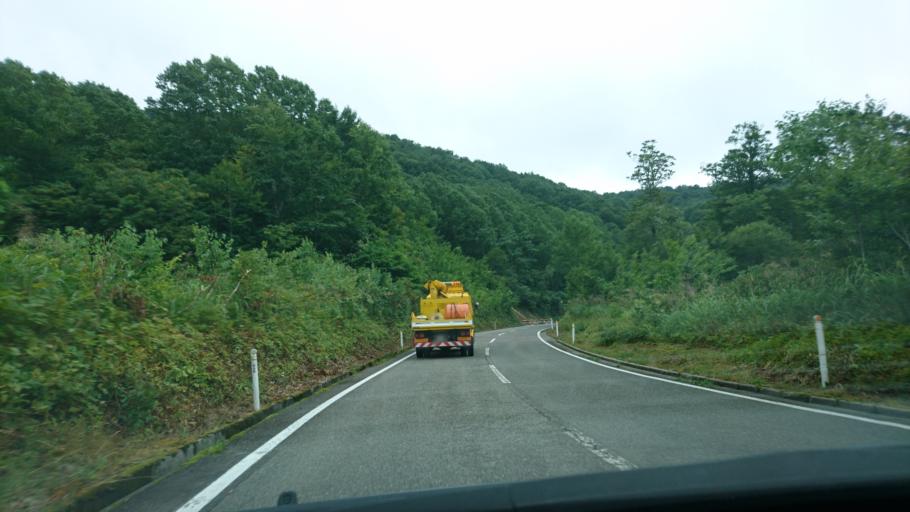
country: JP
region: Akita
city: Yuzawa
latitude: 38.9830
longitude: 140.7376
